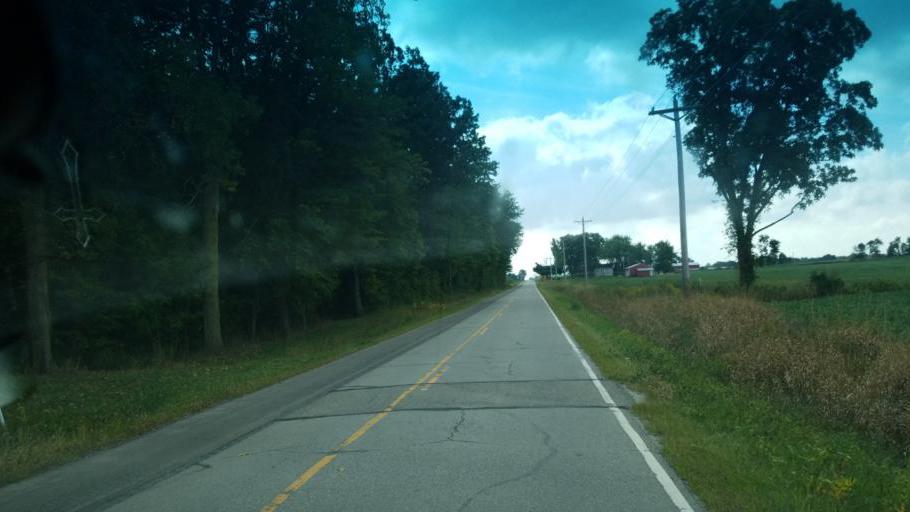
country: US
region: Ohio
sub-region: Crawford County
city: Bucyrus
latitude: 40.9623
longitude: -82.9016
